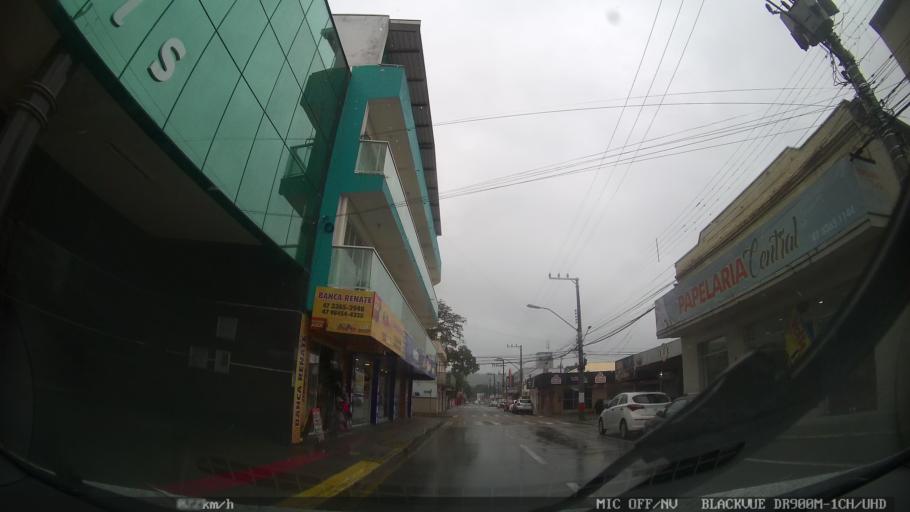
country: BR
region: Santa Catarina
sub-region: Balneario Camboriu
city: Balneario Camboriu
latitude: -27.0232
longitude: -48.6515
